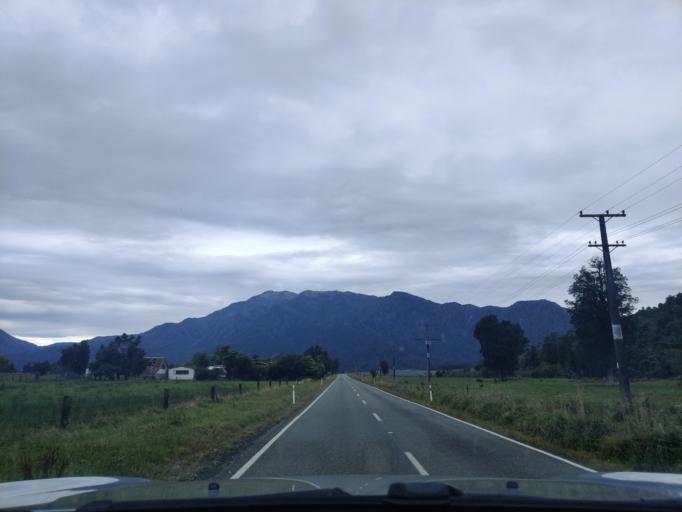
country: NZ
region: West Coast
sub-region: Westland District
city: Hokitika
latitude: -43.1536
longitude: 170.5847
